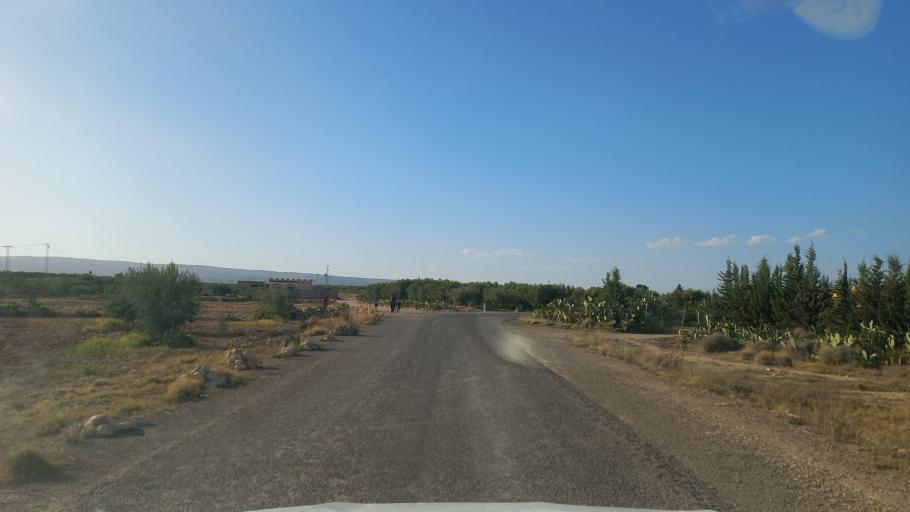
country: TN
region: Al Qasrayn
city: Kasserine
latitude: 35.2661
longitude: 9.0275
